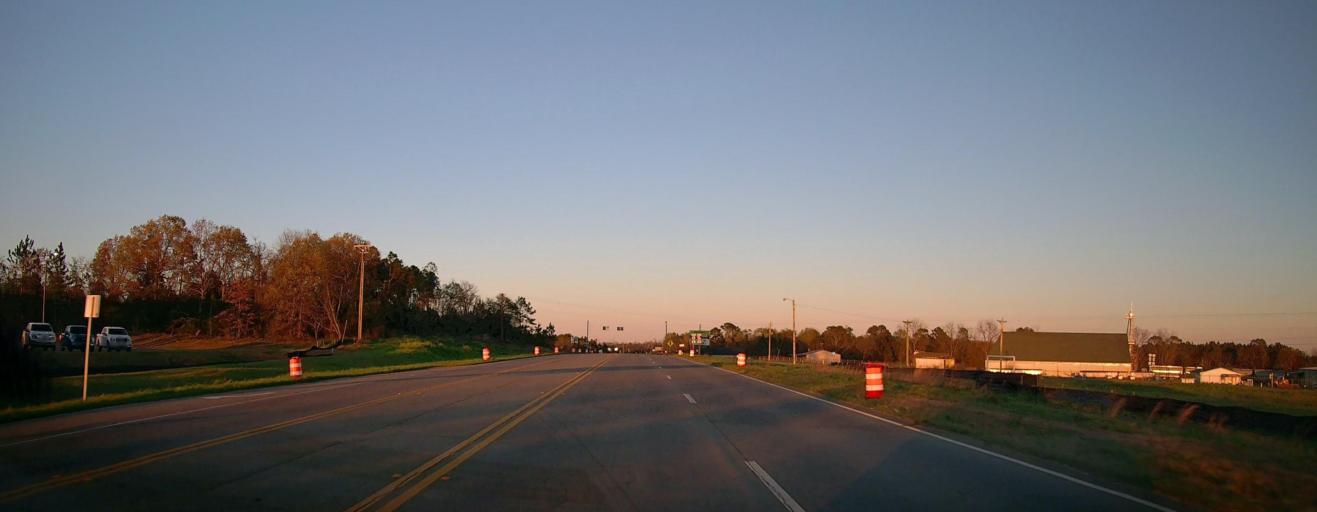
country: US
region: Georgia
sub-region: Crisp County
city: Cordele
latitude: 31.9568
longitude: -83.8079
